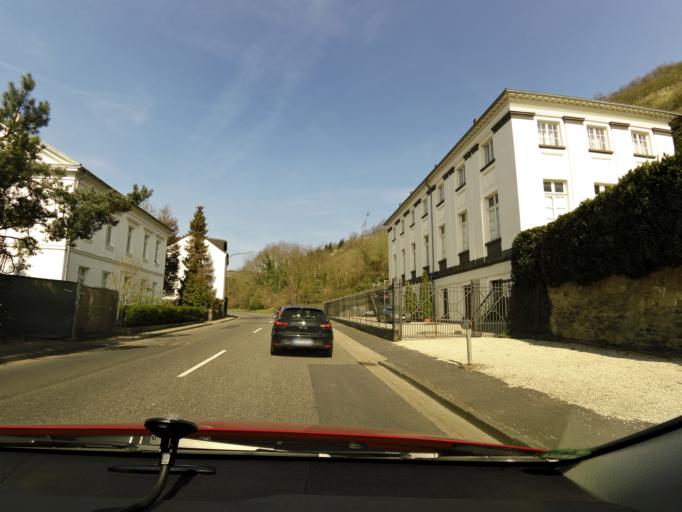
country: DE
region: Rheinland-Pfalz
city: Konigsfeld
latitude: 50.5493
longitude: 7.1693
